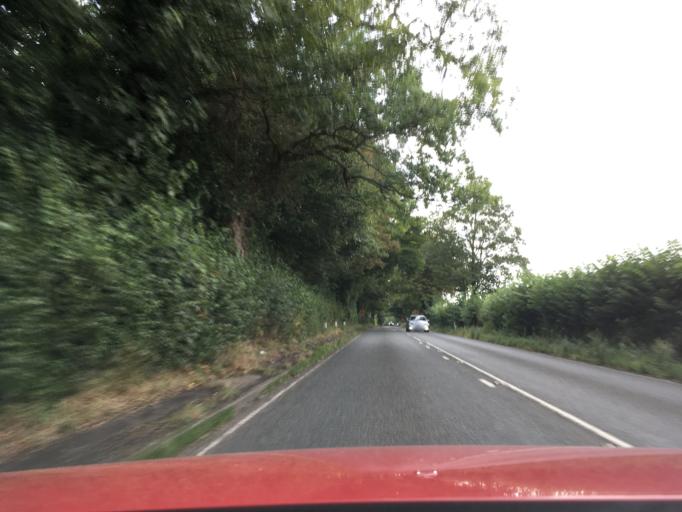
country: GB
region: England
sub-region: Hampshire
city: Kings Worthy
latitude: 51.0959
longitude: -1.2899
